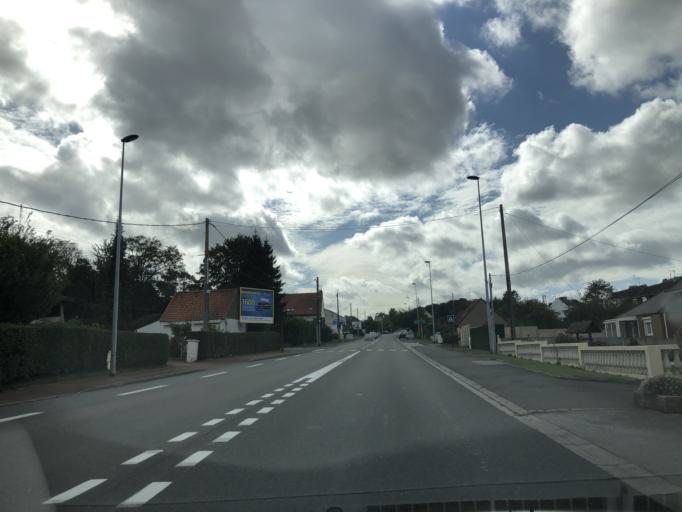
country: FR
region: Nord-Pas-de-Calais
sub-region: Departement du Pas-de-Calais
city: Saint-Omer
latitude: 50.7359
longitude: 2.2544
